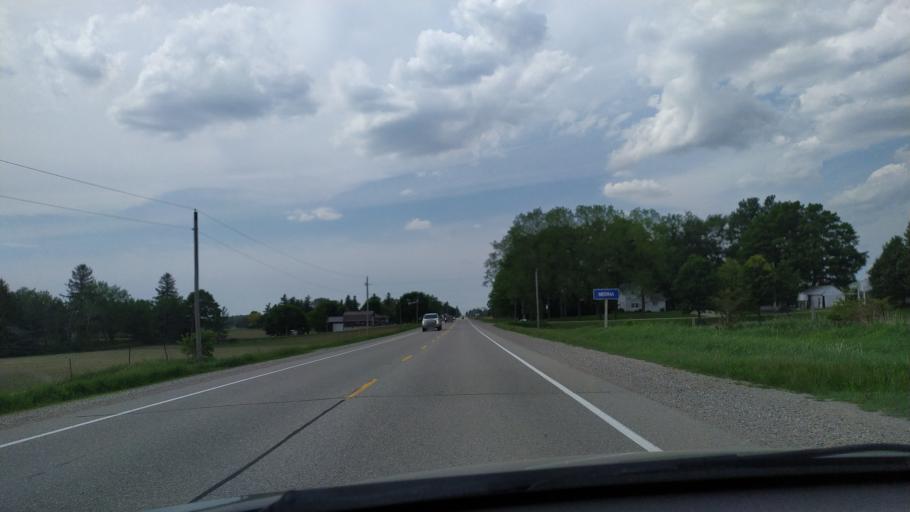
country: CA
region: Ontario
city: Dorchester
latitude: 43.1866
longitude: -81.0543
